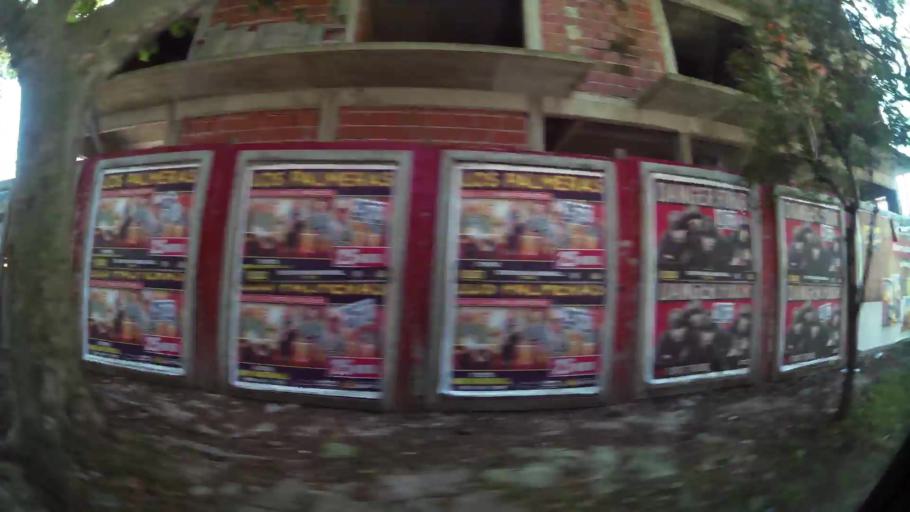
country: AR
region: Buenos Aires
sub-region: Partido de Tigre
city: Tigre
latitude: -34.4267
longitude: -58.5720
